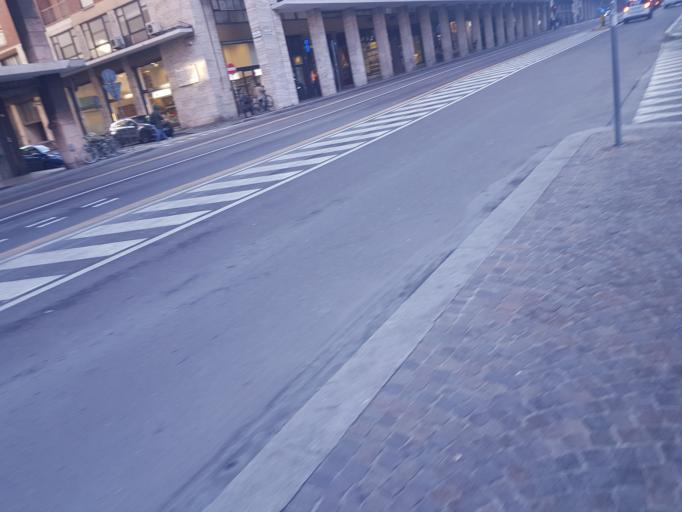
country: IT
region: Emilia-Romagna
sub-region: Provincia di Bologna
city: Bologna
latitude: 44.4999
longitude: 11.3391
